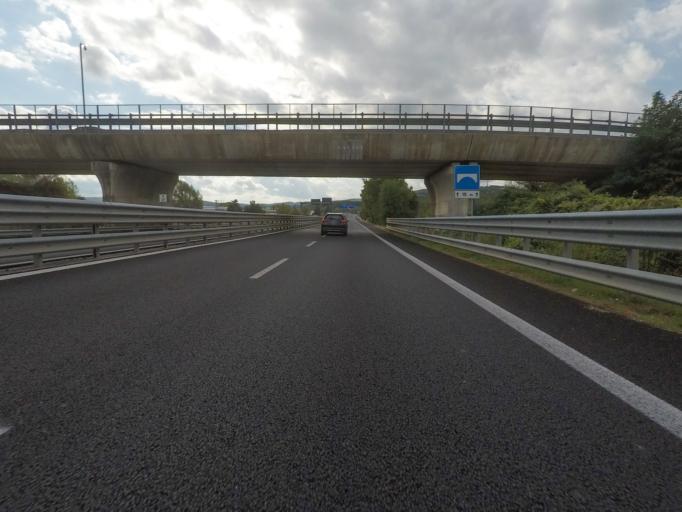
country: IT
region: Tuscany
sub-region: Provincia di Siena
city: Serre di Rapolano
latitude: 43.2713
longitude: 11.6291
